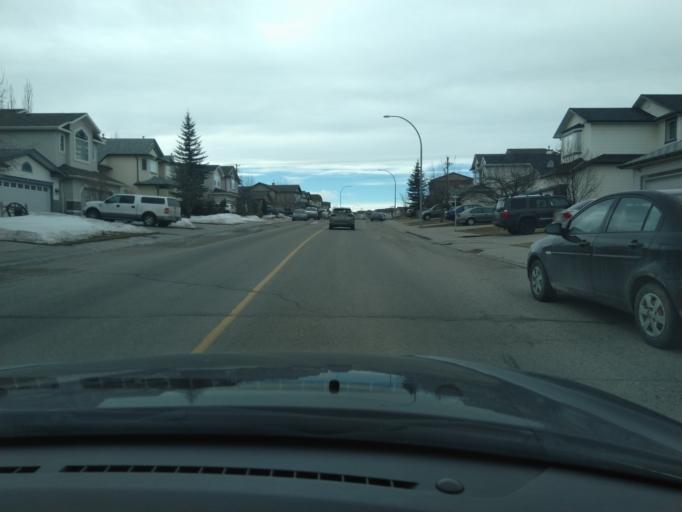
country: CA
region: Alberta
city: Calgary
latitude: 51.1715
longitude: -114.0463
